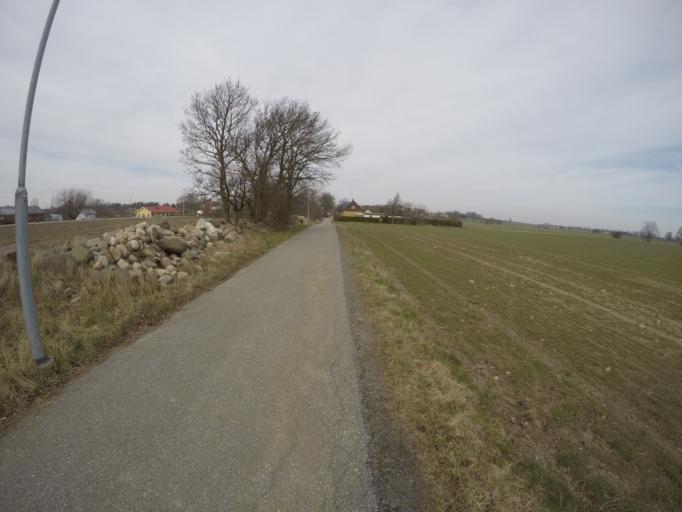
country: SE
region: Skane
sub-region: Ystads Kommun
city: Kopingebro
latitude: 55.4339
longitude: 14.1144
